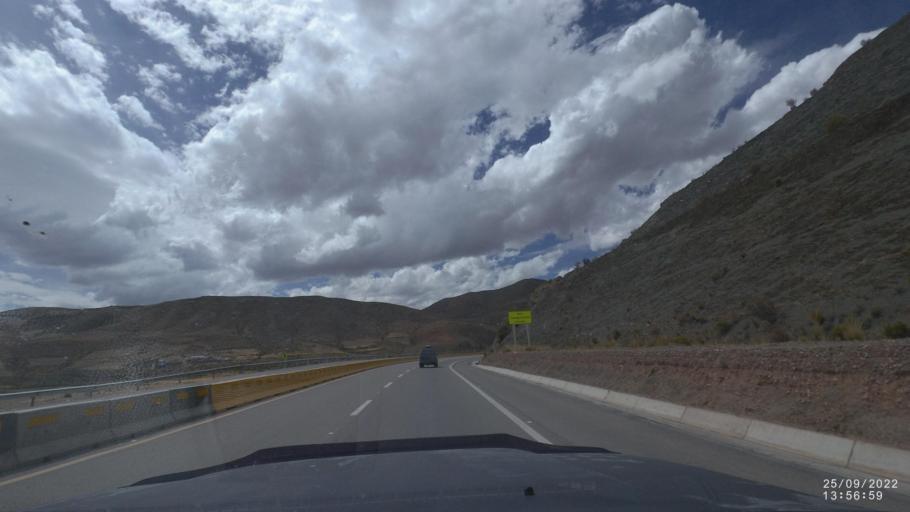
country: BO
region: La Paz
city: Colquiri
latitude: -17.5978
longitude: -66.9599
